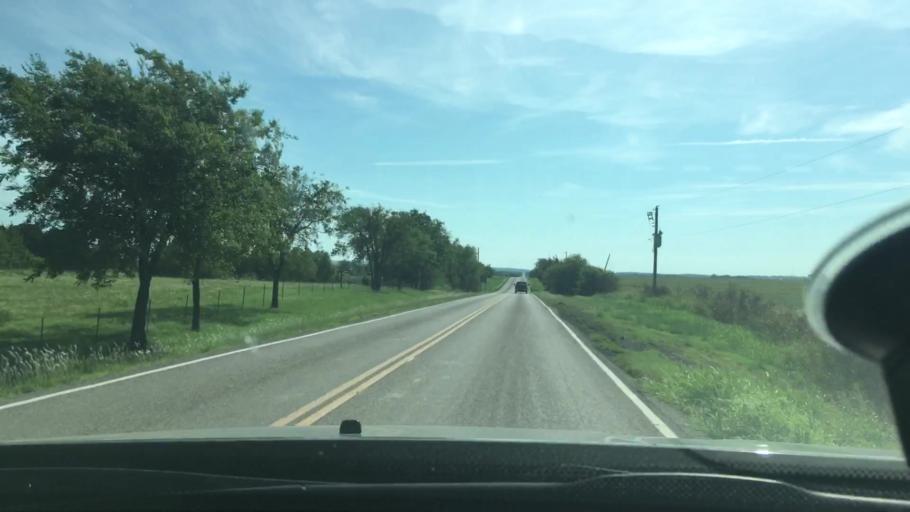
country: US
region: Oklahoma
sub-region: Carter County
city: Lone Grove
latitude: 34.3327
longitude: -97.2210
